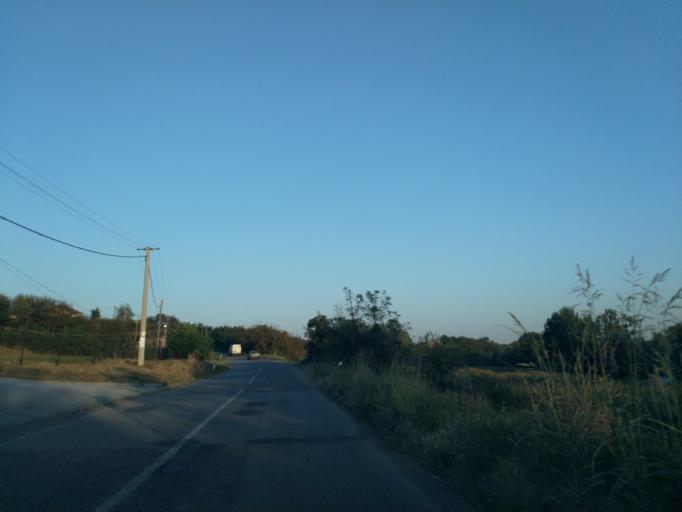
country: RS
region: Central Serbia
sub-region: Rasinski Okrug
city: Trstenik
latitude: 43.6326
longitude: 21.0335
